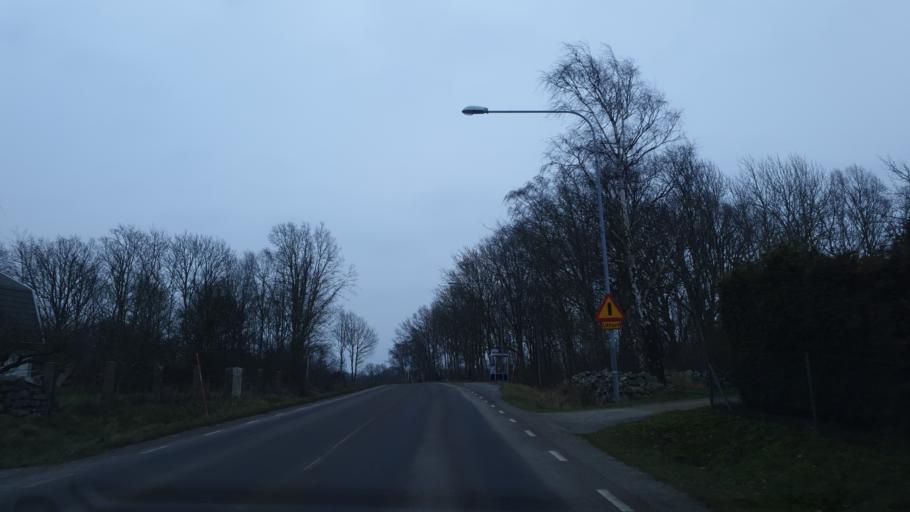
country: SE
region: Blekinge
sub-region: Karlskrona Kommun
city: Sturko
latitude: 56.1140
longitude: 15.6916
